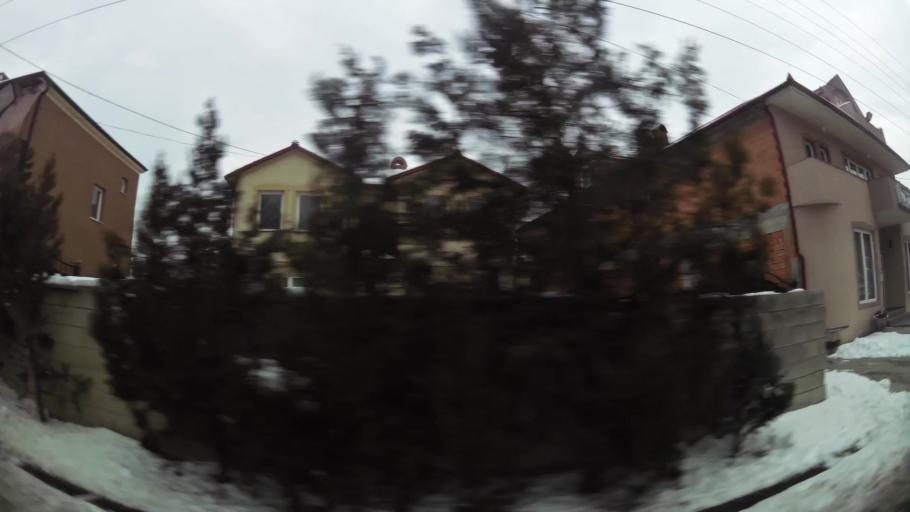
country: MK
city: Kondovo
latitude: 42.0114
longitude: 21.3103
